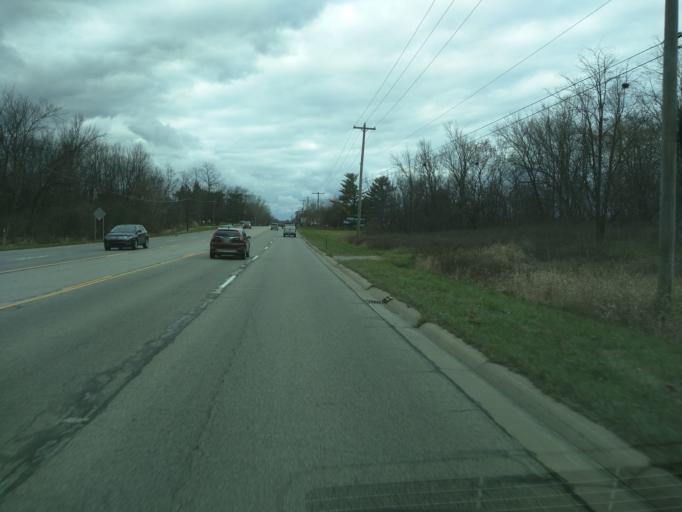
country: US
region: Michigan
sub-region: Ingham County
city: Haslett
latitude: 42.7153
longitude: -84.3961
